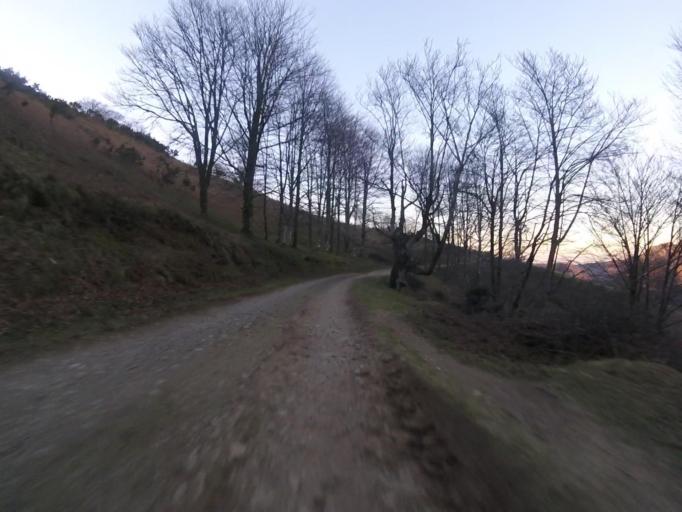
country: ES
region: Navarre
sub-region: Provincia de Navarra
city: Arano
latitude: 43.2546
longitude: -1.8255
